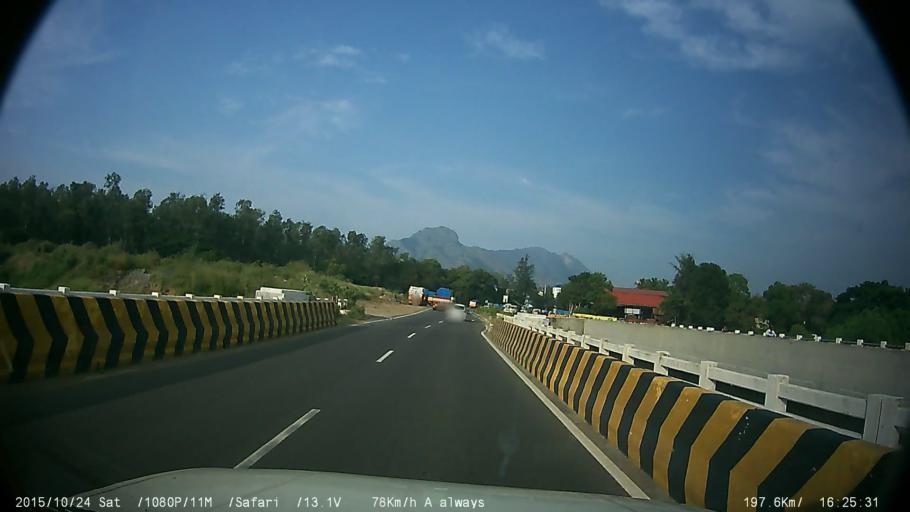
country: IN
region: Kerala
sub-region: Palakkad district
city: Palakkad
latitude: 10.7883
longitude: 76.7193
